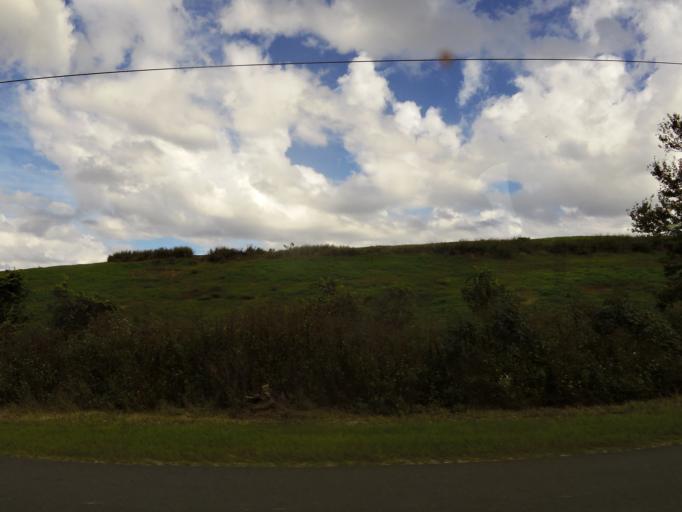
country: US
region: Florida
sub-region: Saint Johns County
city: Villano Beach
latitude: 30.0025
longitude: -81.3997
